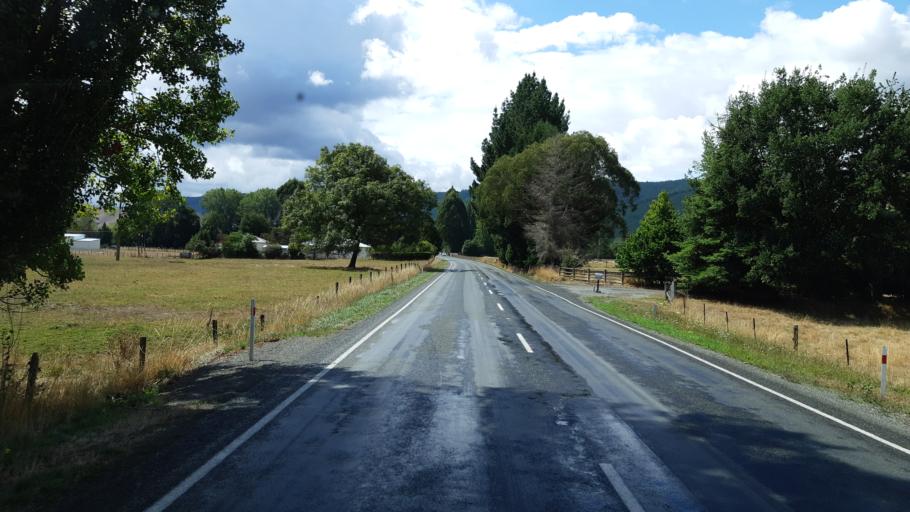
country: NZ
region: Tasman
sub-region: Tasman District
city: Wakefield
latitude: -41.4542
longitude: 172.8164
